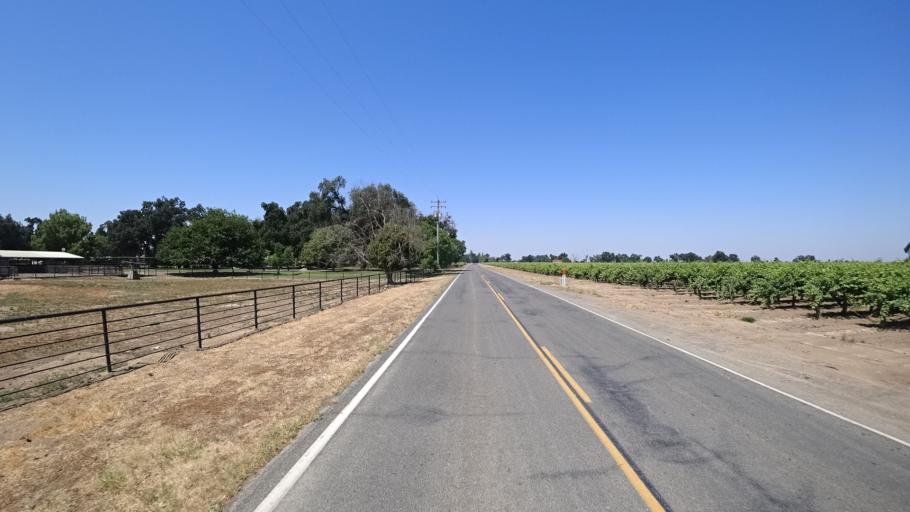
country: US
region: California
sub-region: Kings County
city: Lemoore
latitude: 36.3718
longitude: -119.7816
